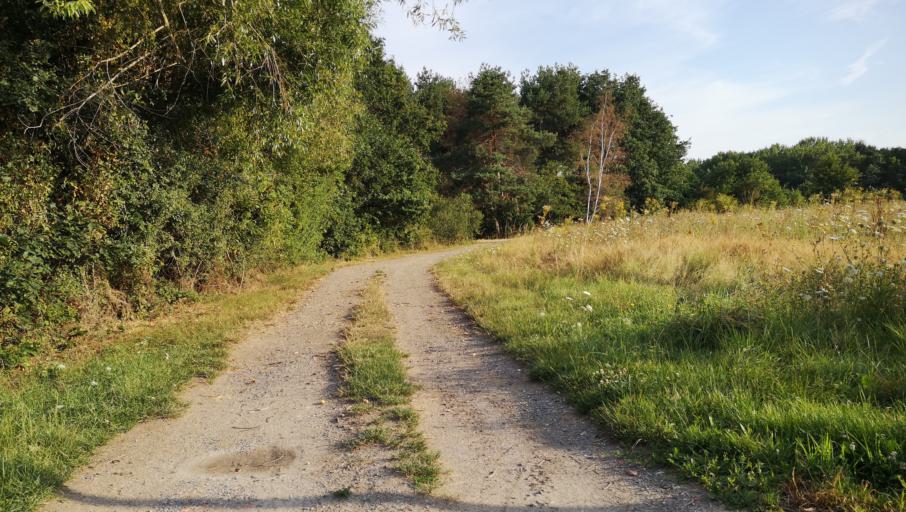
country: FR
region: Centre
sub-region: Departement du Loiret
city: Semoy
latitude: 47.9381
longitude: 1.9584
